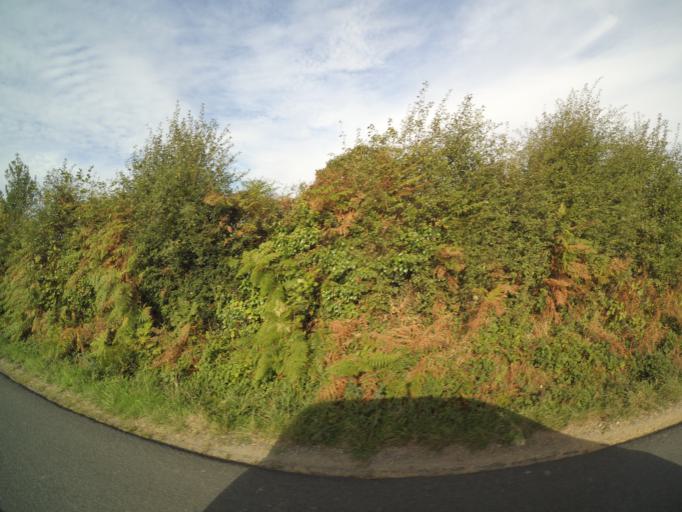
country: FR
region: Pays de la Loire
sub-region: Departement de Maine-et-Loire
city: Tillieres
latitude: 47.1612
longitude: -1.1395
